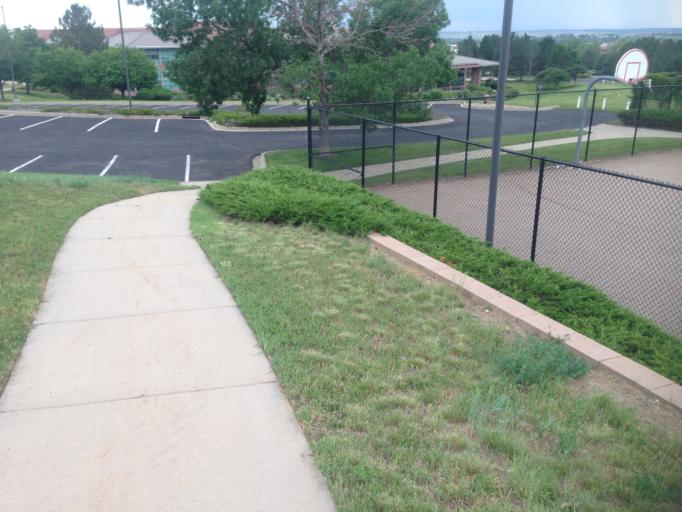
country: US
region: Colorado
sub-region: Boulder County
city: Superior
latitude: 39.9664
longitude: -105.1785
